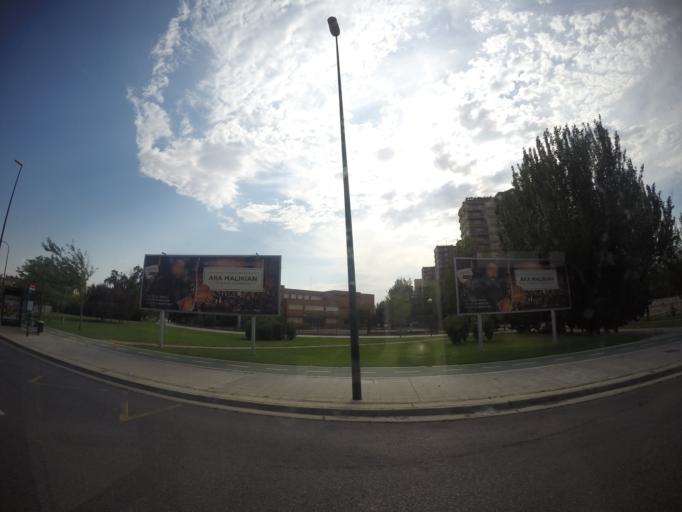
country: ES
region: Aragon
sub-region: Provincia de Zaragoza
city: Zaragoza
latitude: 41.6661
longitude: -0.8810
